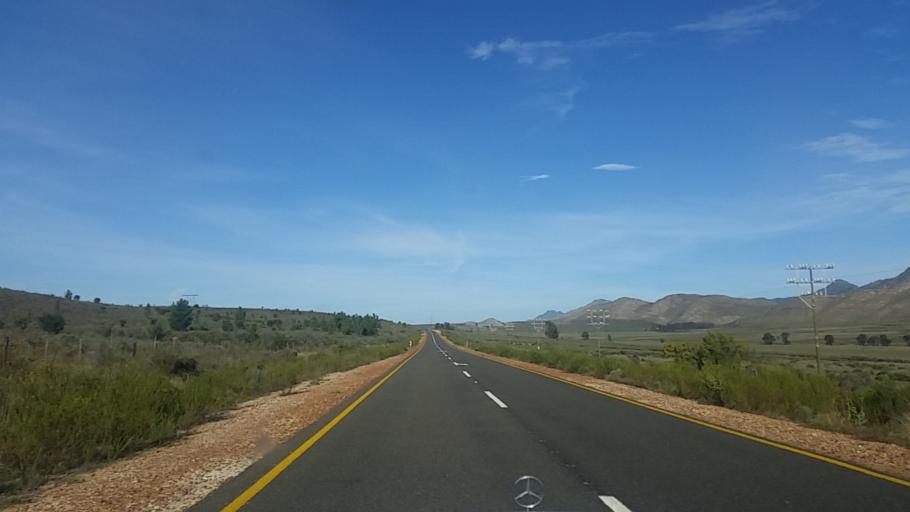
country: ZA
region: Western Cape
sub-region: Eden District Municipality
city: George
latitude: -33.7738
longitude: 22.7438
